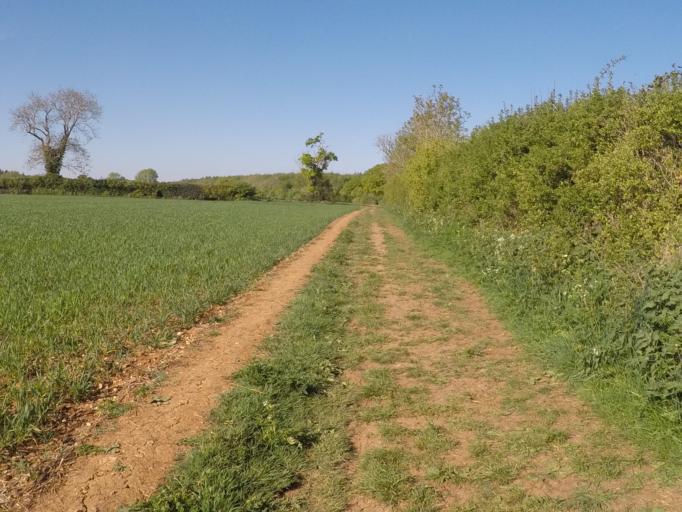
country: GB
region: England
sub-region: Oxfordshire
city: Stonesfield
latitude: 51.8650
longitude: -1.4358
